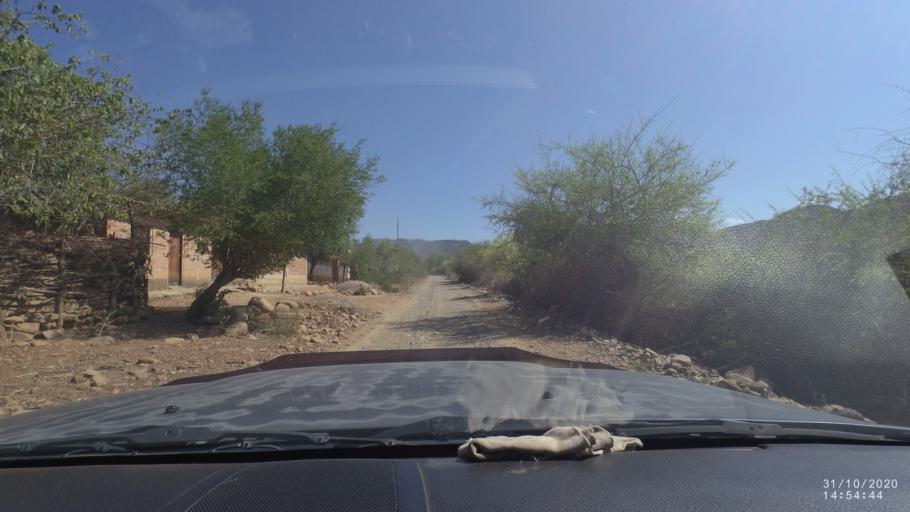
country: BO
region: Cochabamba
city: Aiquile
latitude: -18.2282
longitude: -64.8576
